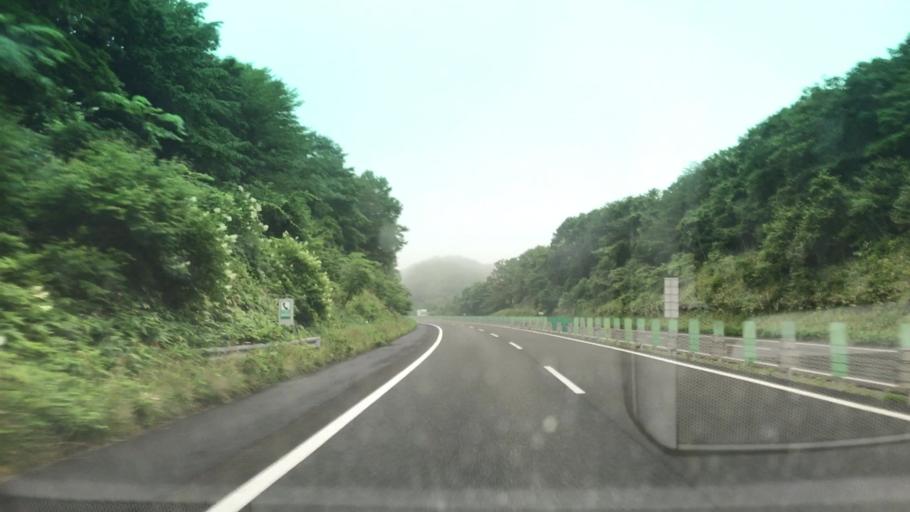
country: JP
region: Hokkaido
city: Shiraoi
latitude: 42.4935
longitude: 141.2420
